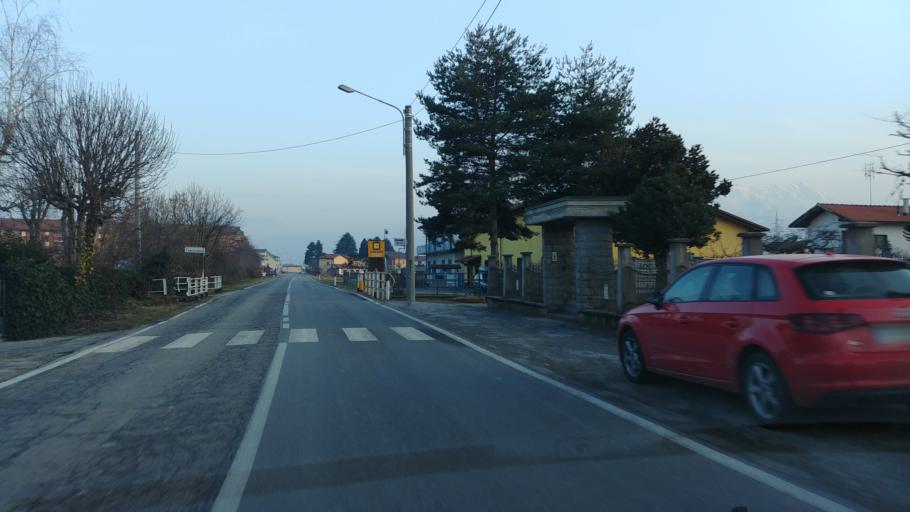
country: IT
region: Piedmont
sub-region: Provincia di Cuneo
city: Cuneo
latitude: 44.4027
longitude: 7.5270
